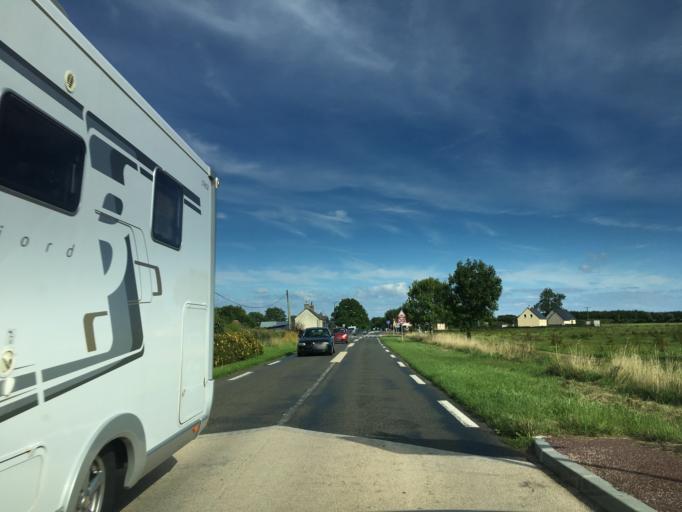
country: FR
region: Lower Normandy
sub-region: Departement du Calvados
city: Cambremer
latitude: 49.1415
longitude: 0.0335
